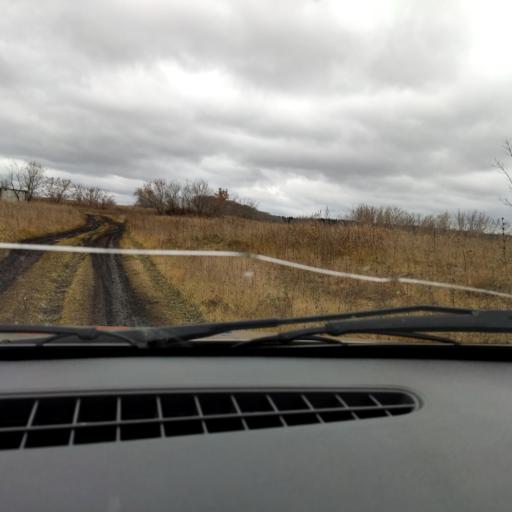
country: RU
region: Bashkortostan
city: Kabakovo
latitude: 54.4773
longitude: 55.9144
